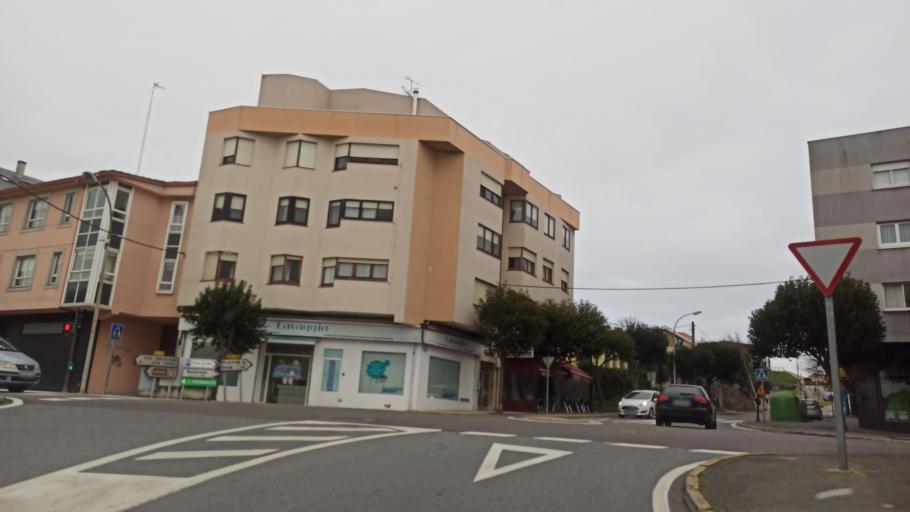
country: ES
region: Galicia
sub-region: Provincia da Coruna
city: Cambre
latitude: 43.3324
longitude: -8.3713
